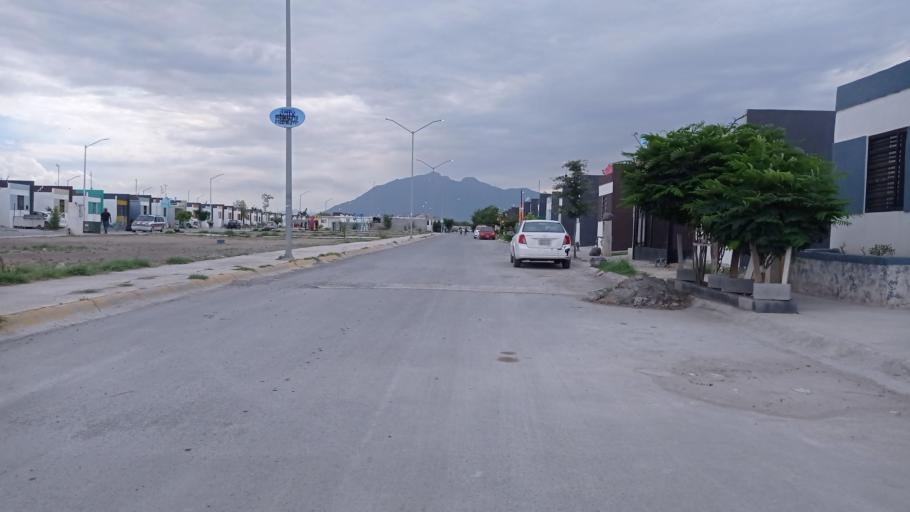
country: MX
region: Nuevo Leon
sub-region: Salinas Victoria
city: Simeprodeso (Colectivo Nuevo)
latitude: 25.8742
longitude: -100.3168
